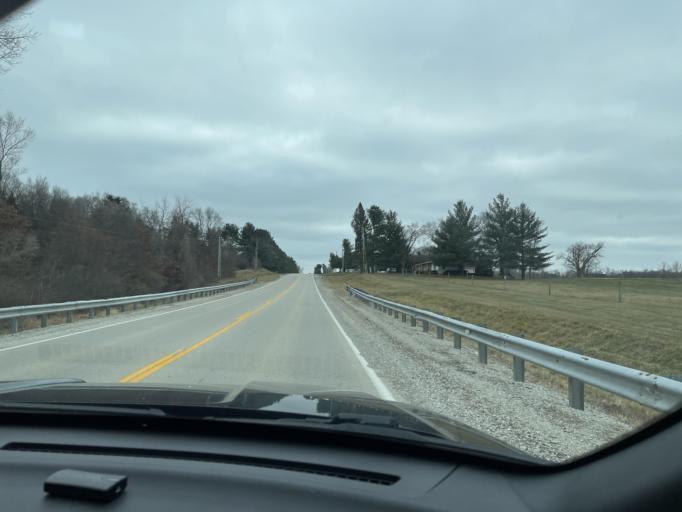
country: US
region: Illinois
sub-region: Sangamon County
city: Leland Grove
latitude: 39.8097
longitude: -89.7394
